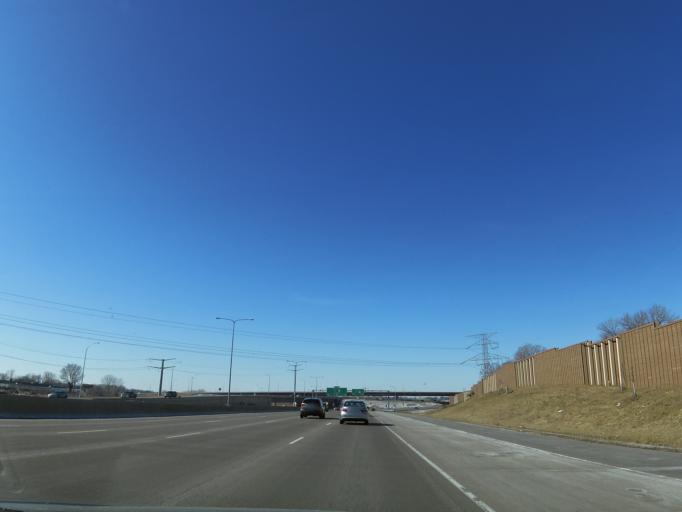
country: US
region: Minnesota
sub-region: Ramsey County
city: Little Canada
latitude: 45.0360
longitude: -93.0826
